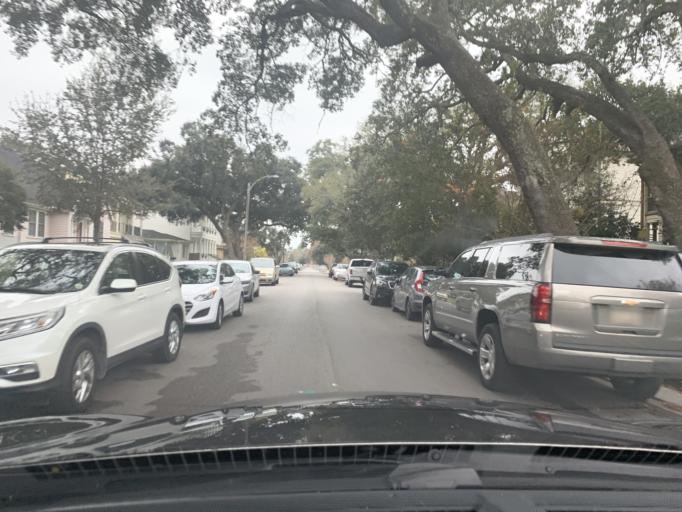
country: US
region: Louisiana
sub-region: Jefferson Parish
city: Metairie
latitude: 30.0158
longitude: -90.1091
